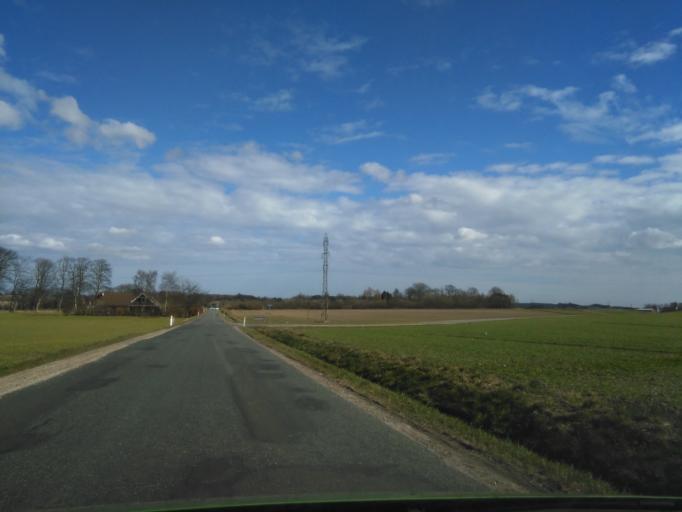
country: DK
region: Central Jutland
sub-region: Skanderborg Kommune
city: Skanderborg
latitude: 55.9177
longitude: 9.9746
